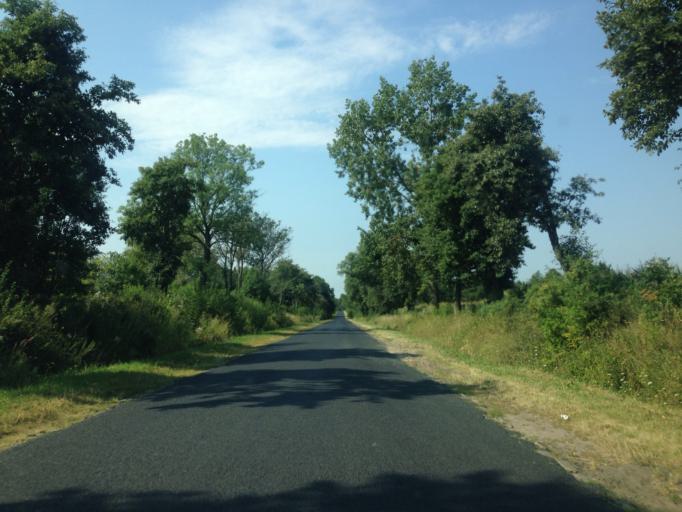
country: PL
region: Kujawsko-Pomorskie
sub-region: Powiat rypinski
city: Rypin
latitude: 53.0991
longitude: 19.4465
